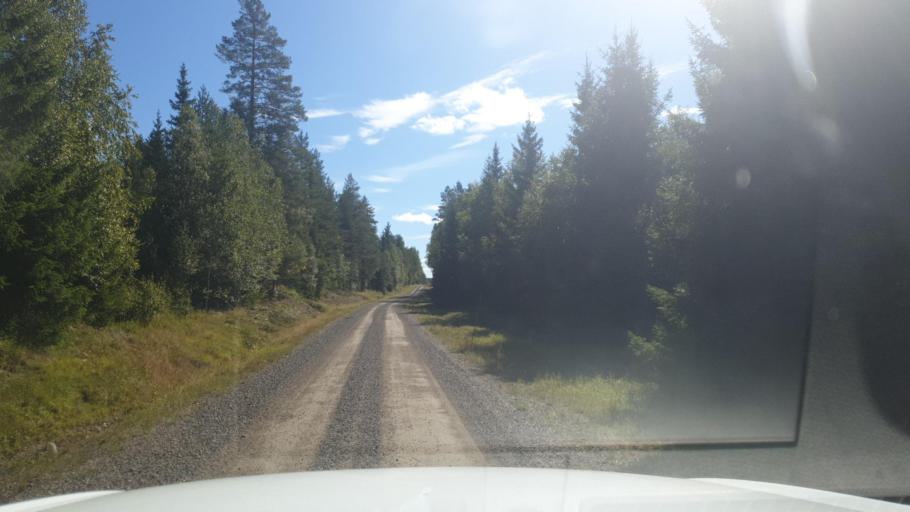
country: SE
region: Vaermland
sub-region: Eda Kommun
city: Charlottenberg
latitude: 60.1246
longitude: 12.5979
